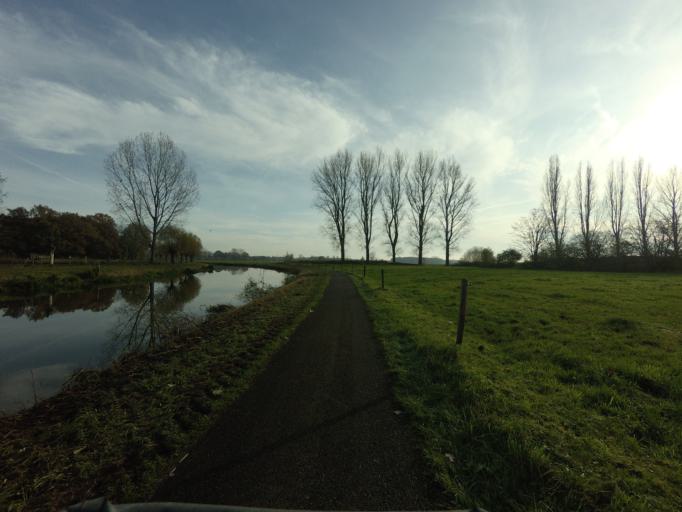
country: NL
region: North Brabant
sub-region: Gemeente Breda
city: Breda
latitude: 51.5283
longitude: 4.7791
